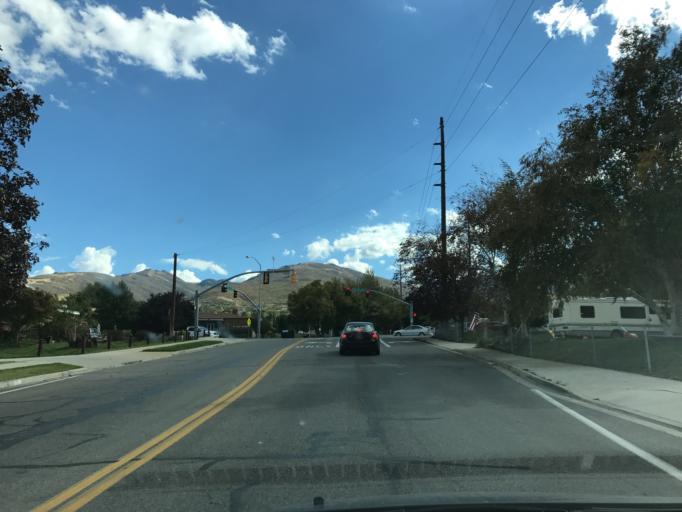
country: US
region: Utah
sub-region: Davis County
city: Woods Cross
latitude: 40.8711
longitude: -111.8775
